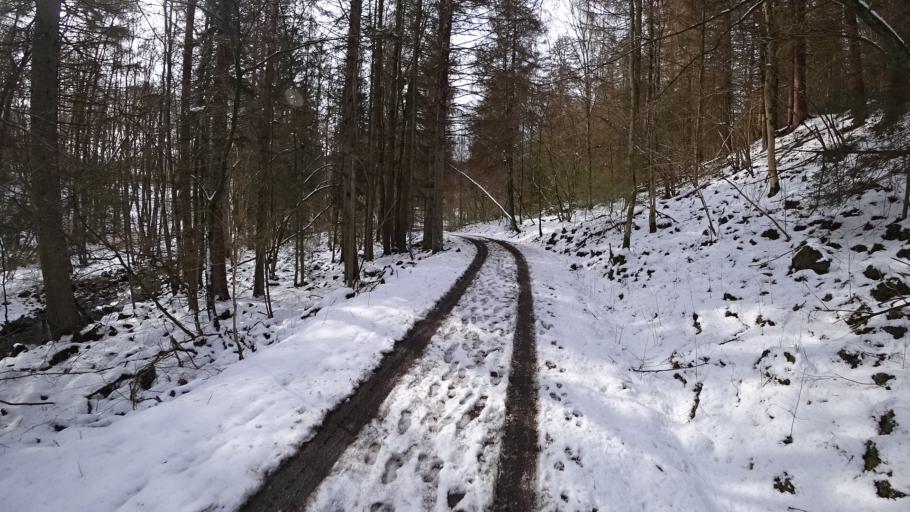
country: DE
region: Rheinland-Pfalz
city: Nauroth
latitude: 50.6902
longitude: 7.8748
